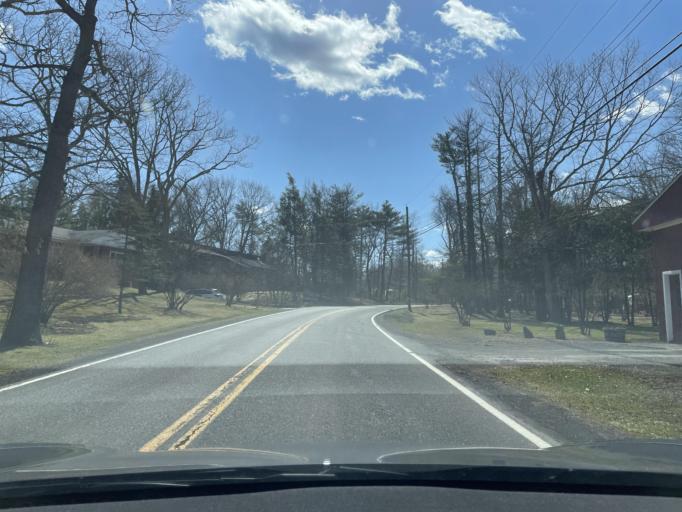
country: US
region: New York
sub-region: Ulster County
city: West Hurley
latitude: 41.9654
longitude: -74.0995
